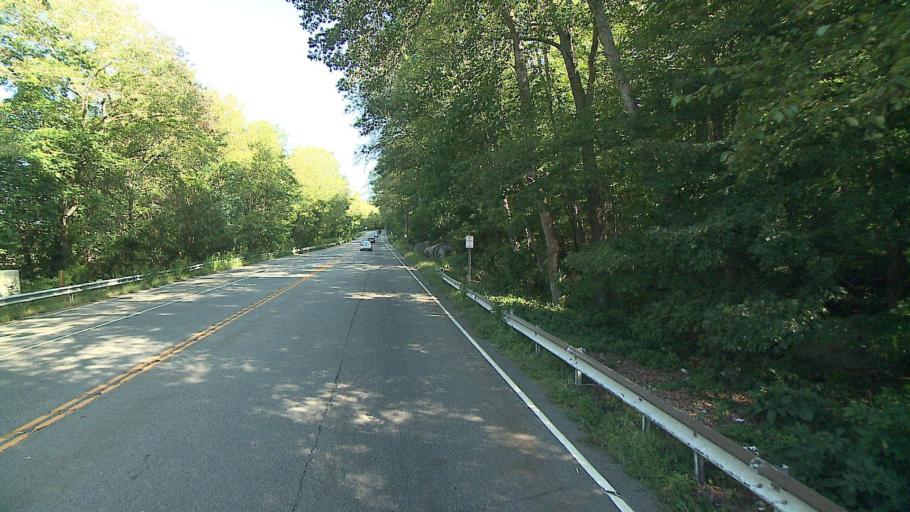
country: US
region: Connecticut
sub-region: New London County
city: Conning Towers-Nautilus Park
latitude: 41.3984
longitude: -72.0805
